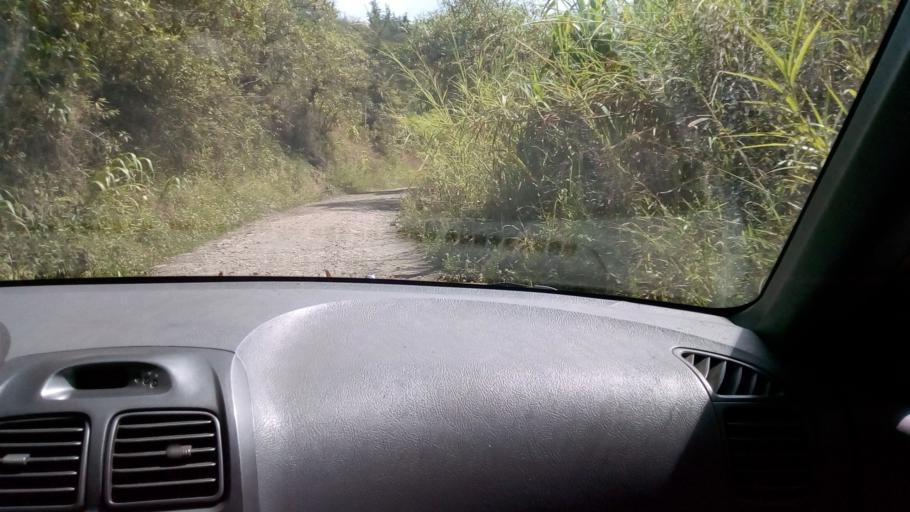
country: CO
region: Cundinamarca
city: Tenza
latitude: 5.0955
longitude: -73.4219
